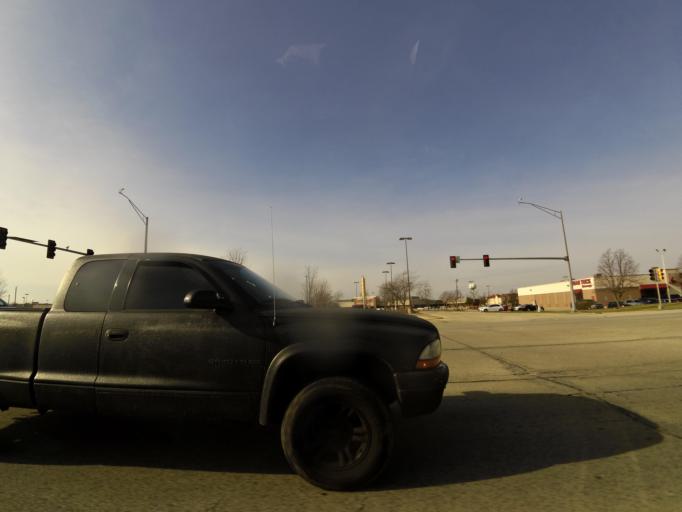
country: US
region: Illinois
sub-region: Macon County
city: Forsyth
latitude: 39.9193
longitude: -88.9554
